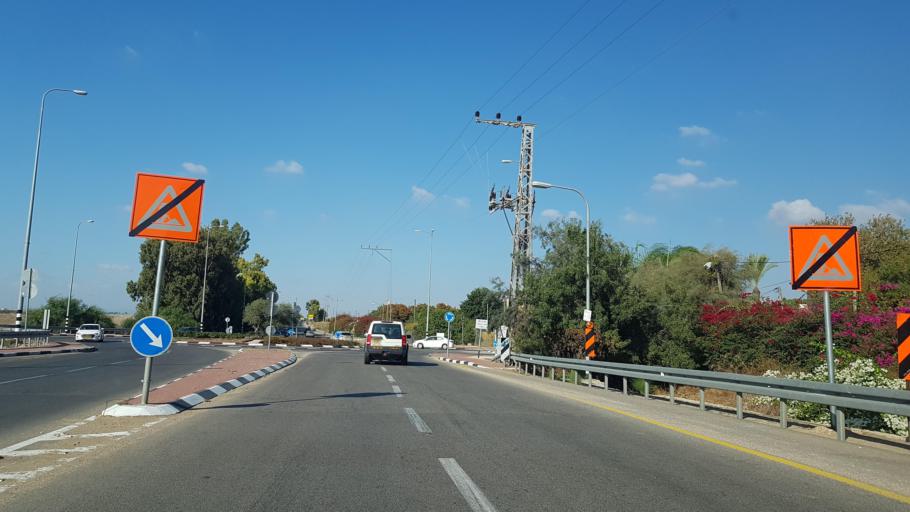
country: PS
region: West Bank
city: Tulkarm
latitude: 32.3375
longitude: 35.0092
